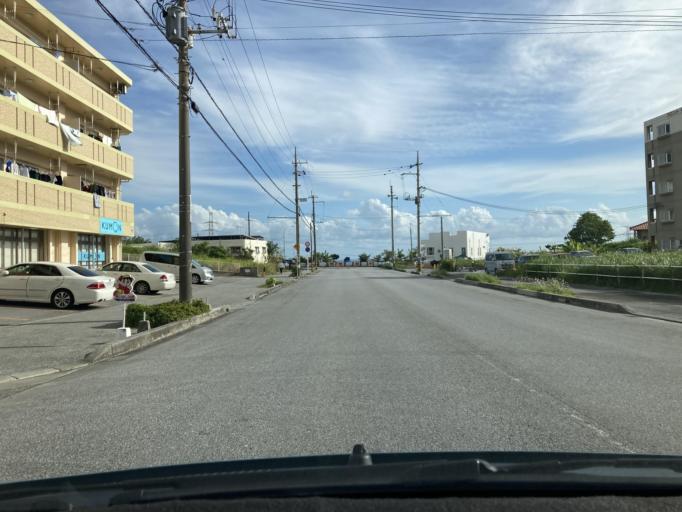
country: JP
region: Okinawa
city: Okinawa
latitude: 26.3390
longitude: 127.8257
